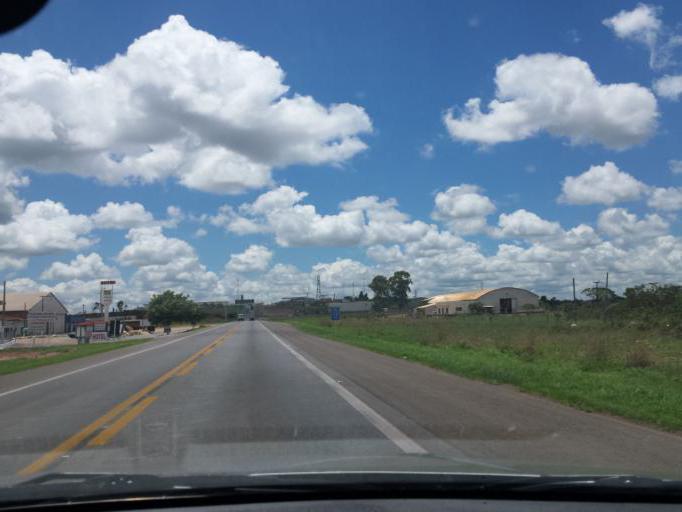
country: BR
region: Goias
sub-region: Cristalina
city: Cristalina
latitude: -16.7433
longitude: -47.6137
